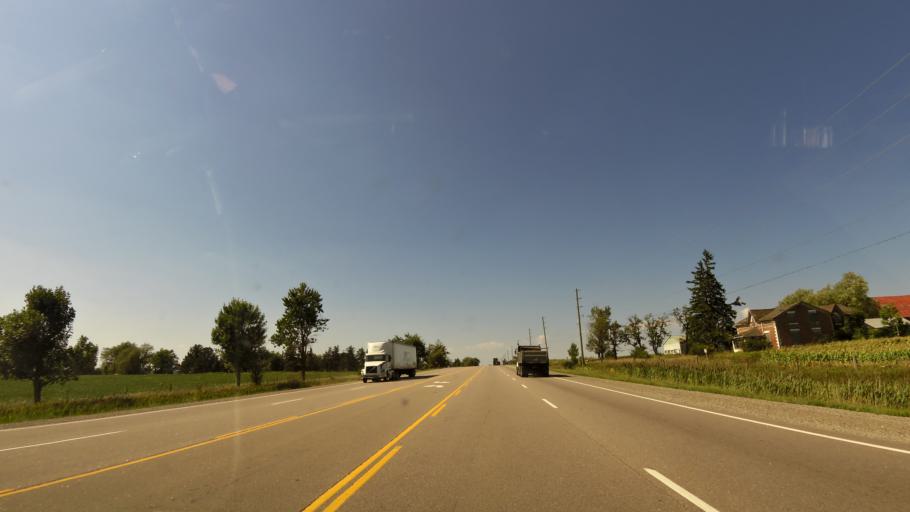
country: CA
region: Ontario
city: Brampton
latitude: 43.7618
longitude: -79.8625
